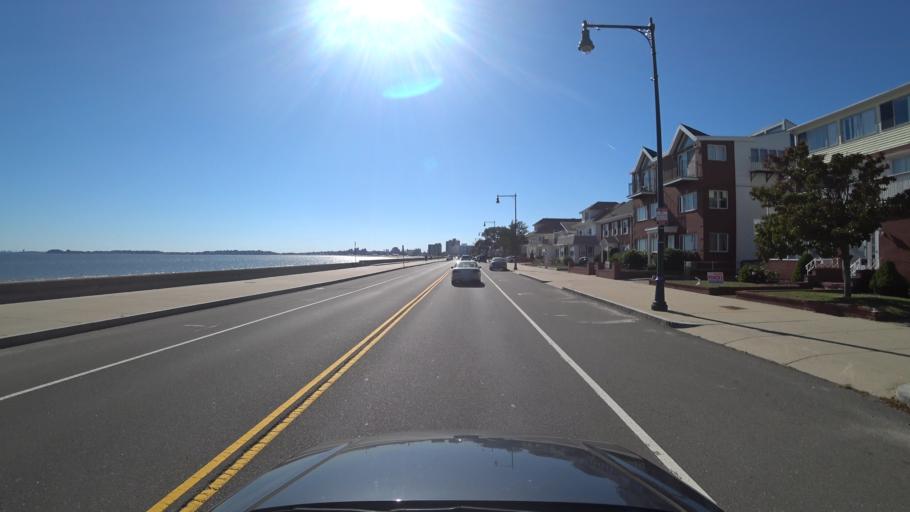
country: US
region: Massachusetts
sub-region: Essex County
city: Lynn
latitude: 42.4344
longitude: -70.9717
